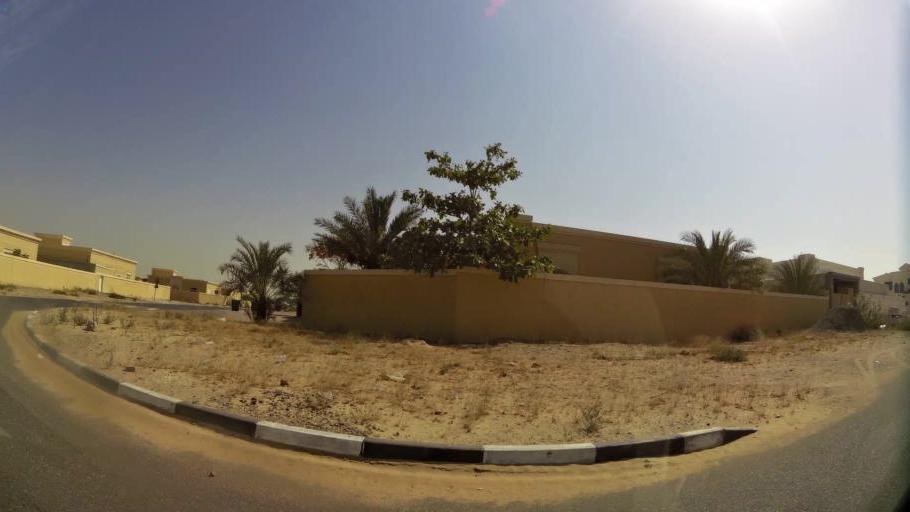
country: AE
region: Ajman
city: Ajman
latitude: 25.4139
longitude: 55.5422
